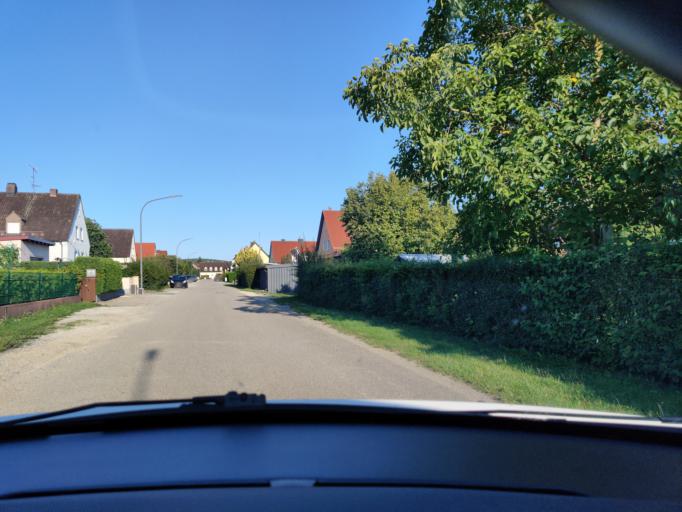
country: DE
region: Bavaria
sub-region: Upper Palatinate
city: Schwarzenfeld
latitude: 49.3879
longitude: 12.1262
